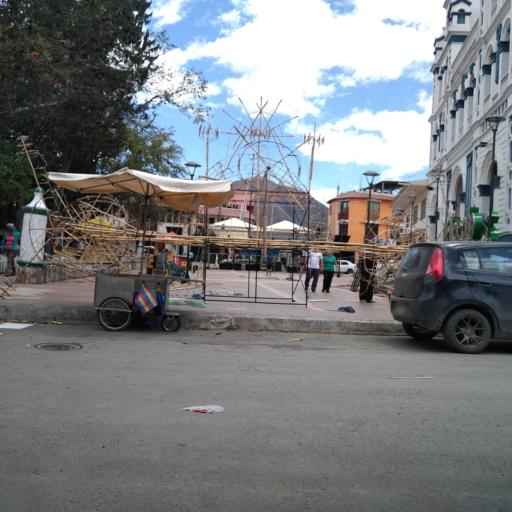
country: EC
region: Loja
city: Loja
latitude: -4.2190
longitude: -79.2585
